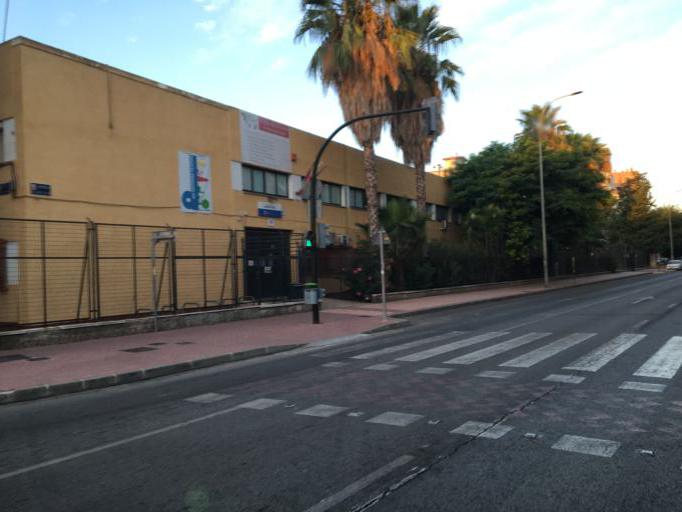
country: ES
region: Murcia
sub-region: Murcia
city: Murcia
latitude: 37.9804
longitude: -1.1193
